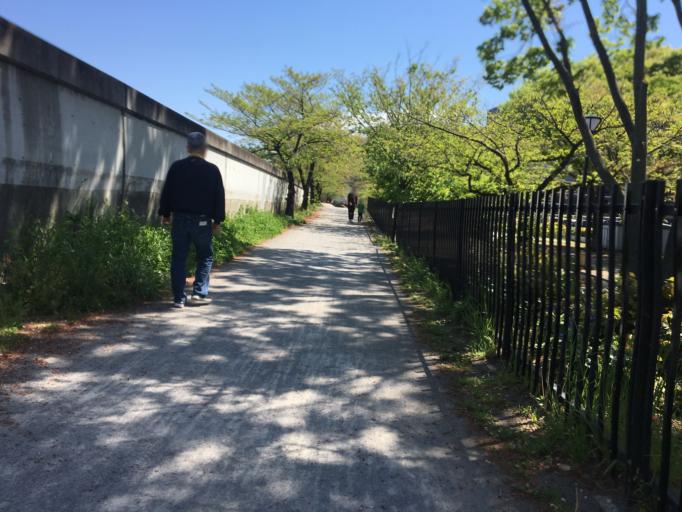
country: JP
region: Saitama
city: Shimotoda
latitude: 35.7910
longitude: 139.6741
